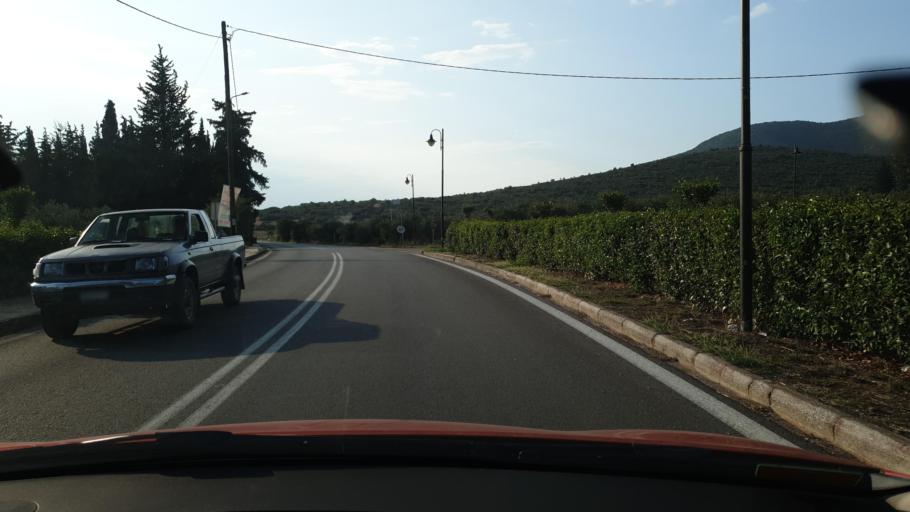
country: GR
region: Thessaly
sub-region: Nomos Magnisias
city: Sourpi
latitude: 39.1080
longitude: 22.8906
